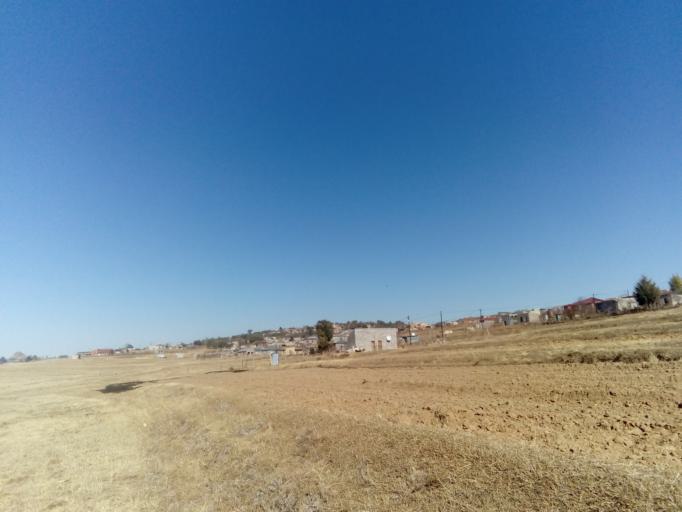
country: LS
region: Berea
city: Teyateyaneng
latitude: -29.1404
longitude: 27.7696
